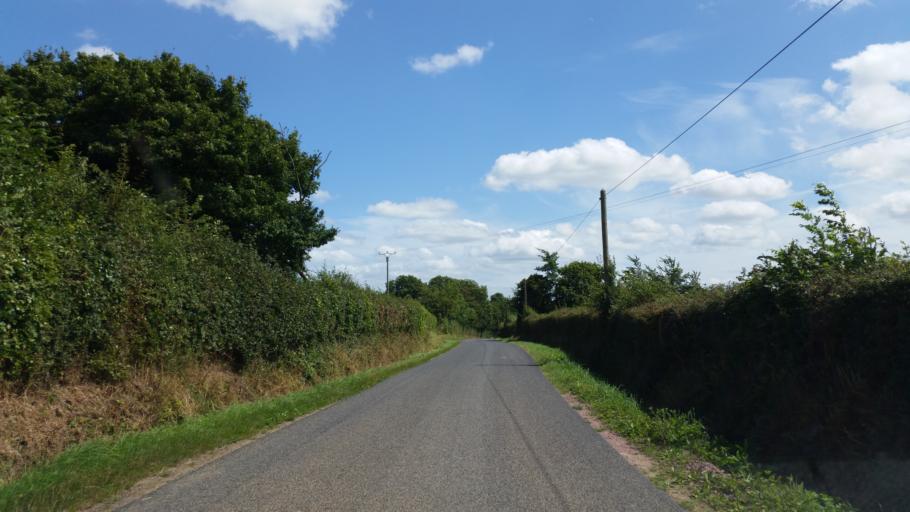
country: FR
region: Lower Normandy
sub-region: Departement de la Manche
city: Montebourg
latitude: 49.4642
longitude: -1.3347
